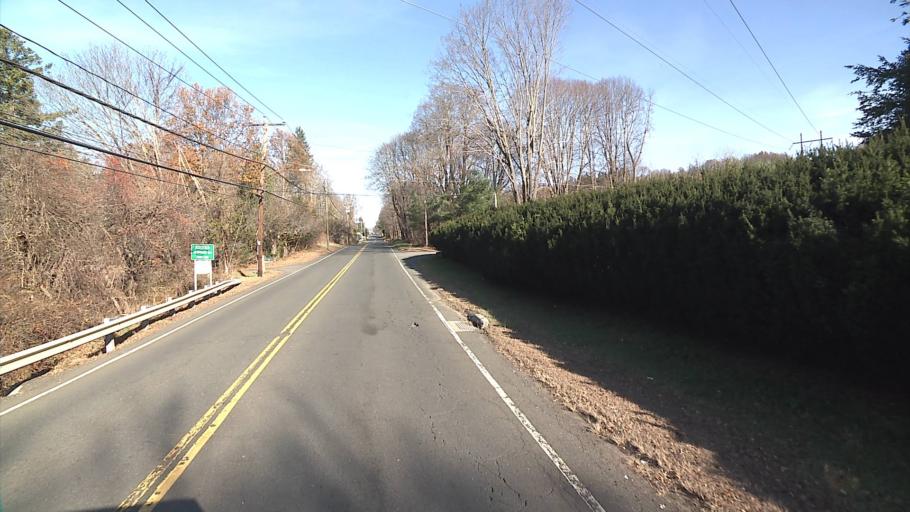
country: US
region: Connecticut
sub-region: Middlesex County
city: Durham
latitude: 41.4945
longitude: -72.6792
